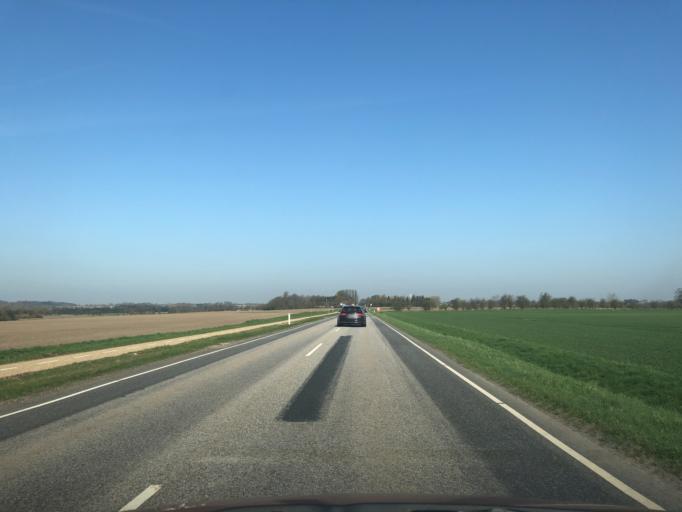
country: DK
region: Zealand
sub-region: Ringsted Kommune
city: Ringsted
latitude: 55.3696
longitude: 11.8635
